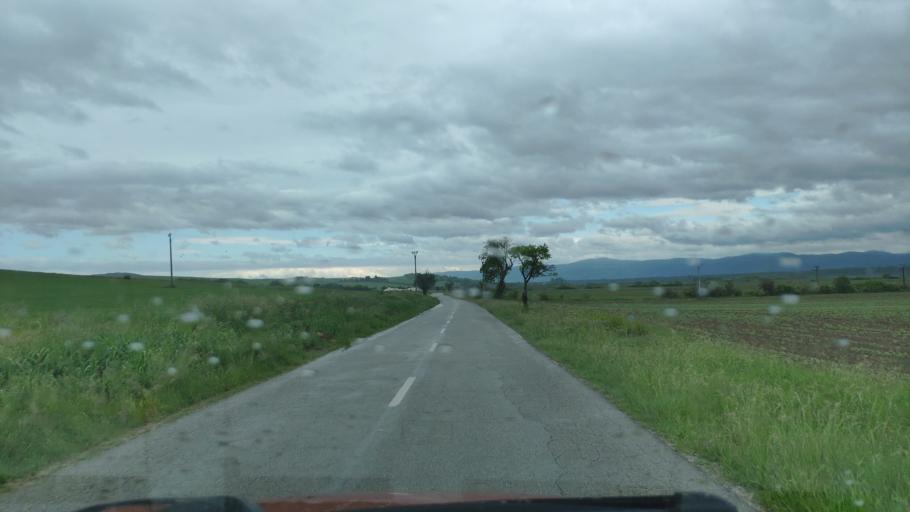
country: SK
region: Kosicky
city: Moldava nad Bodvou
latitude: 48.5364
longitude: 21.0718
